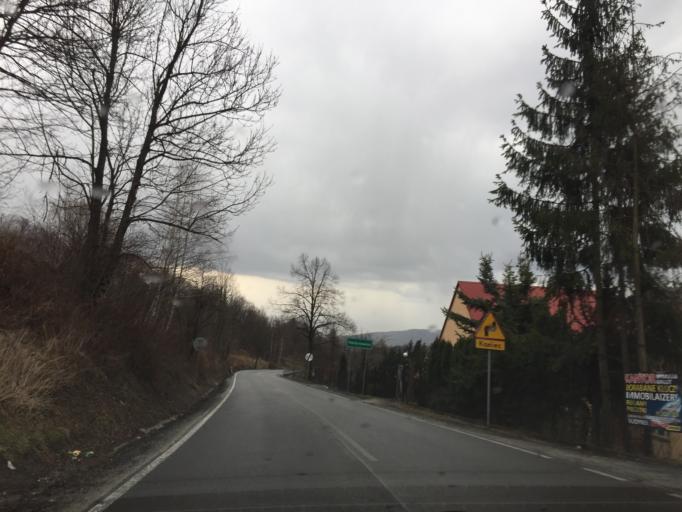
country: PL
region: Lesser Poland Voivodeship
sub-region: Powiat myslenicki
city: Harbutowice
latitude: 49.8046
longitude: 19.7681
